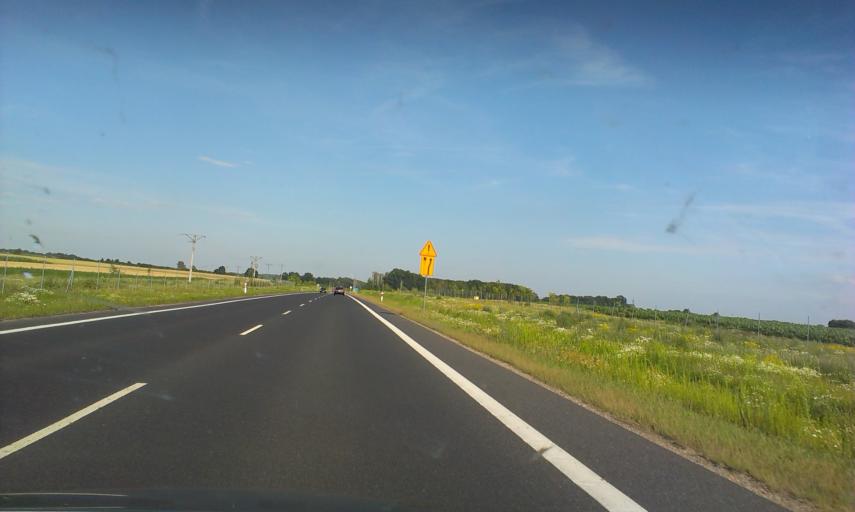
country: PL
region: Greater Poland Voivodeship
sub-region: Powiat pilski
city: Wyrzysk
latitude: 53.1610
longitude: 17.2858
